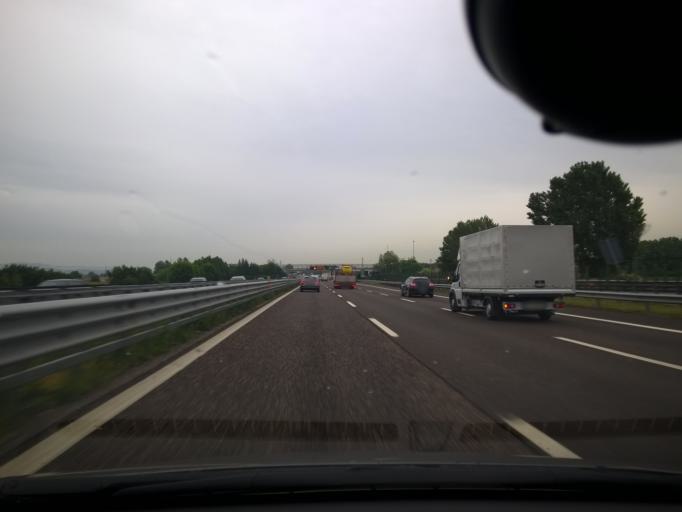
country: IT
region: Veneto
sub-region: Provincia di Verona
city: San Giovanni Lupatoto
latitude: 45.4046
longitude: 11.0588
